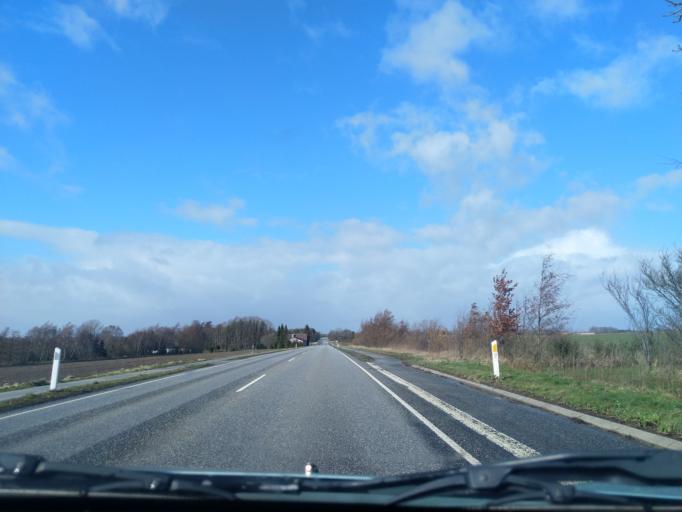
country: DK
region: Zealand
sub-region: Naestved Kommune
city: Naestved
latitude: 55.2797
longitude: 11.7200
